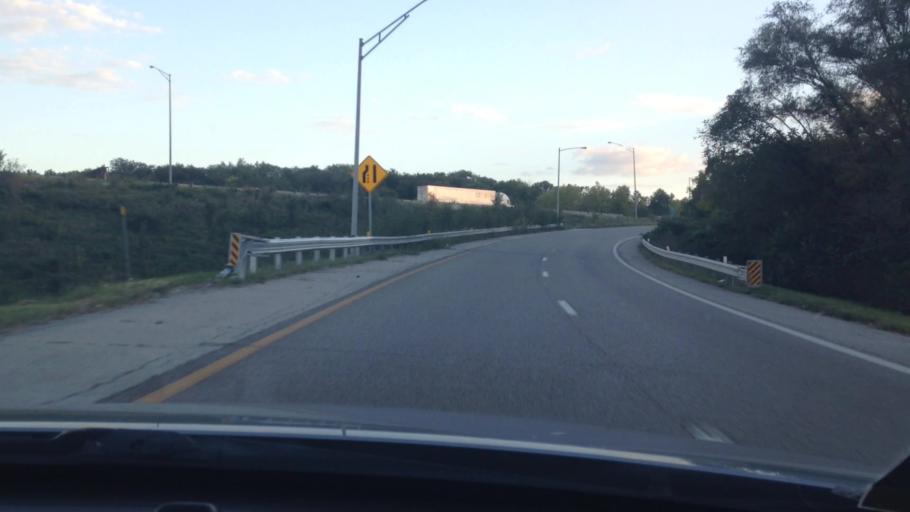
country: US
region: Missouri
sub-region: Jackson County
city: Raytown
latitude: 39.0588
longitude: -94.4926
